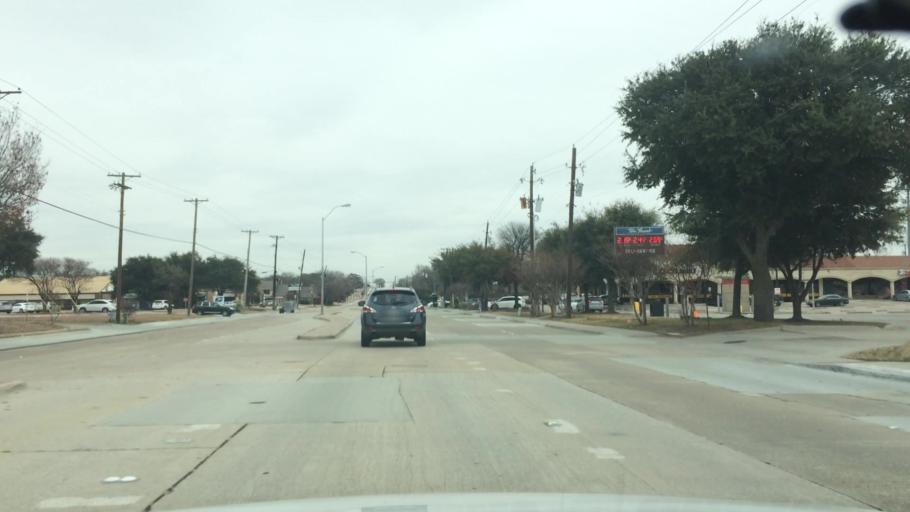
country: US
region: Texas
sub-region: Collin County
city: Plano
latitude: 33.0410
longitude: -96.7523
